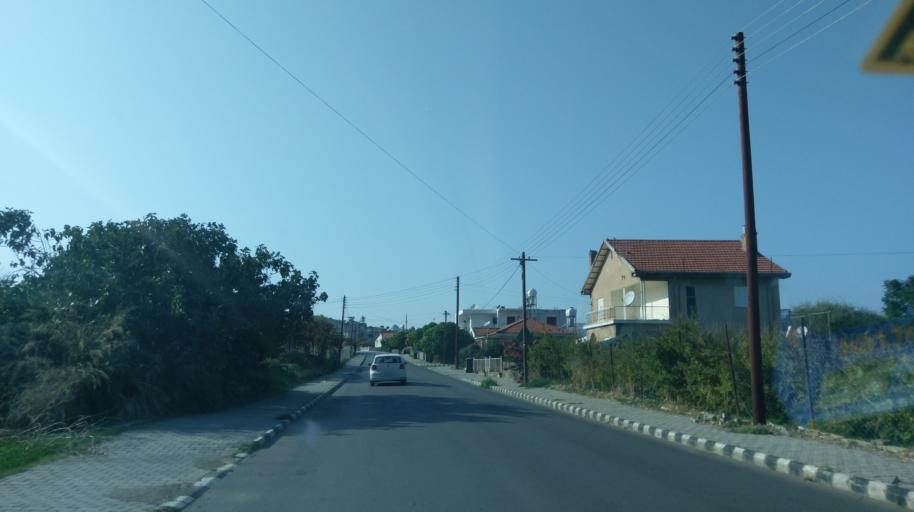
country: CY
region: Lefkosia
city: Lefka
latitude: 35.1427
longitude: 32.8127
